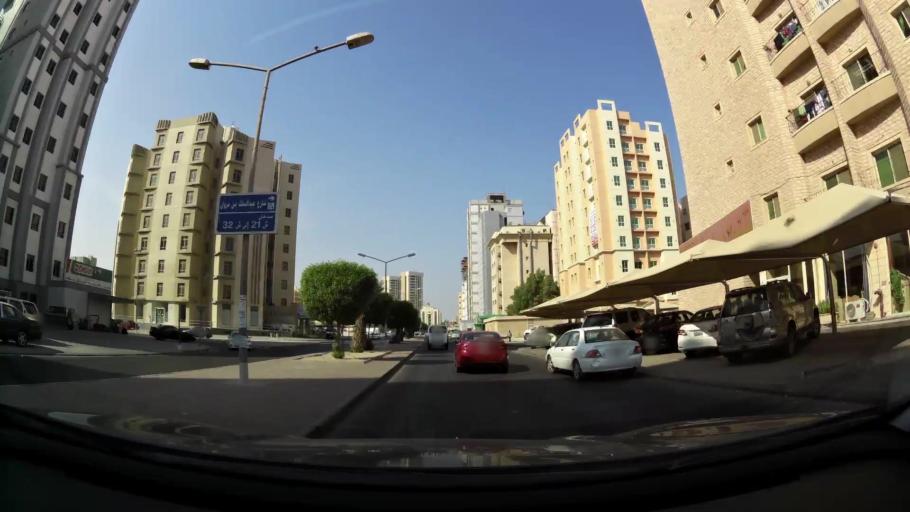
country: KW
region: Al Ahmadi
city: Al Mahbulah
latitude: 29.1343
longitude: 48.1227
